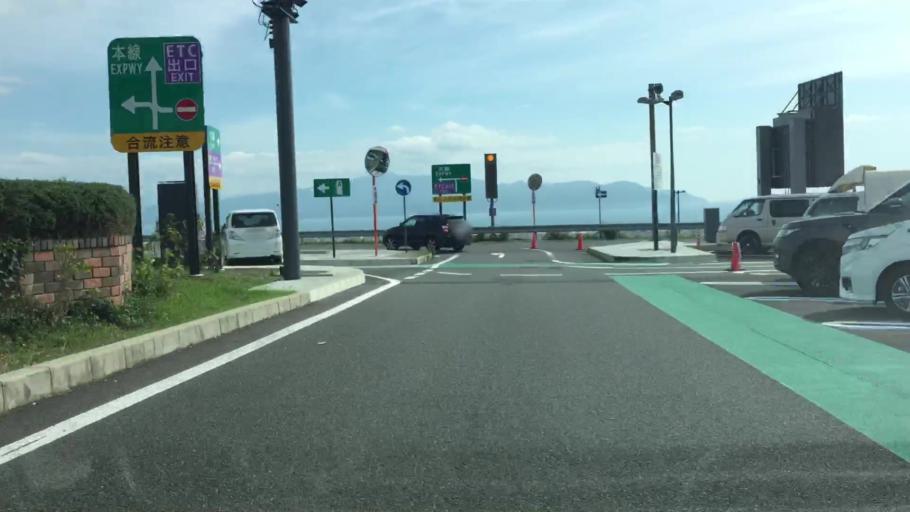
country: JP
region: Shizuoka
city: Numazu
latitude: 35.1541
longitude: 138.8062
